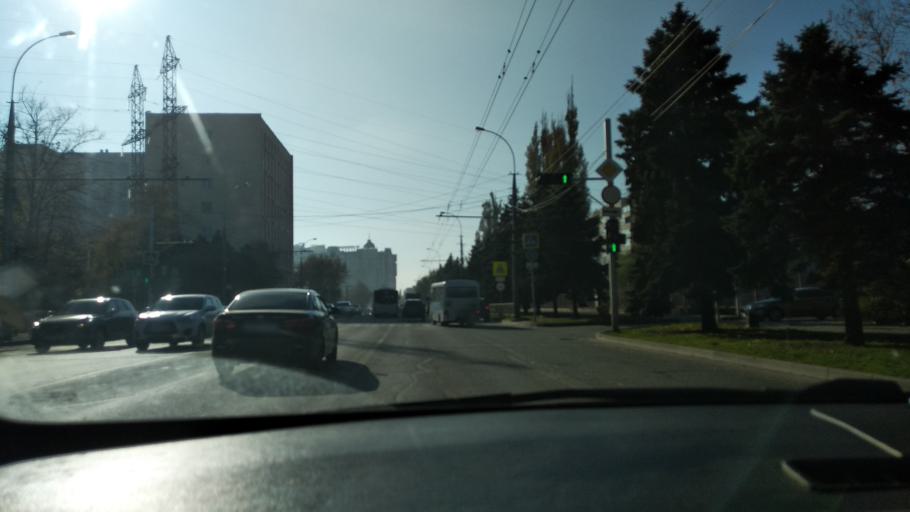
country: RU
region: Krasnodarskiy
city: Pashkovskiy
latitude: 45.0194
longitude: 39.0490
